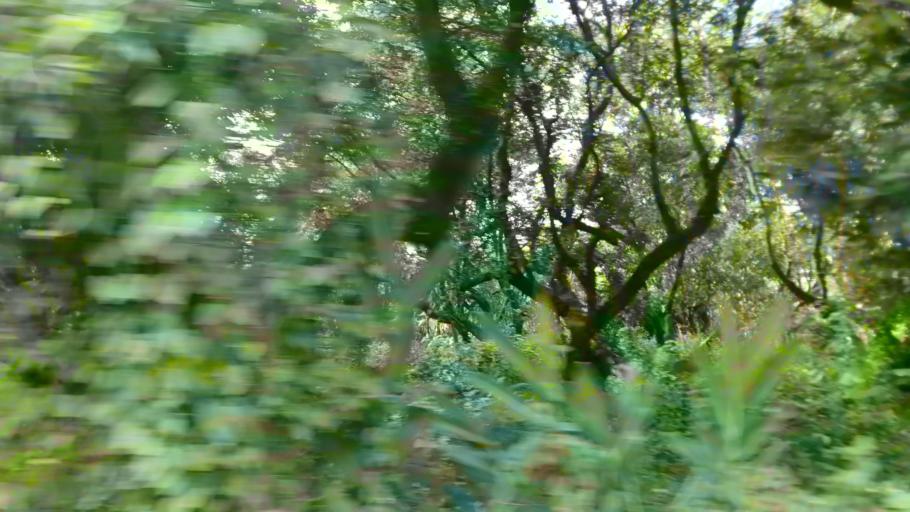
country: TW
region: Taiwan
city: Yujing
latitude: 23.0479
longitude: 120.4009
